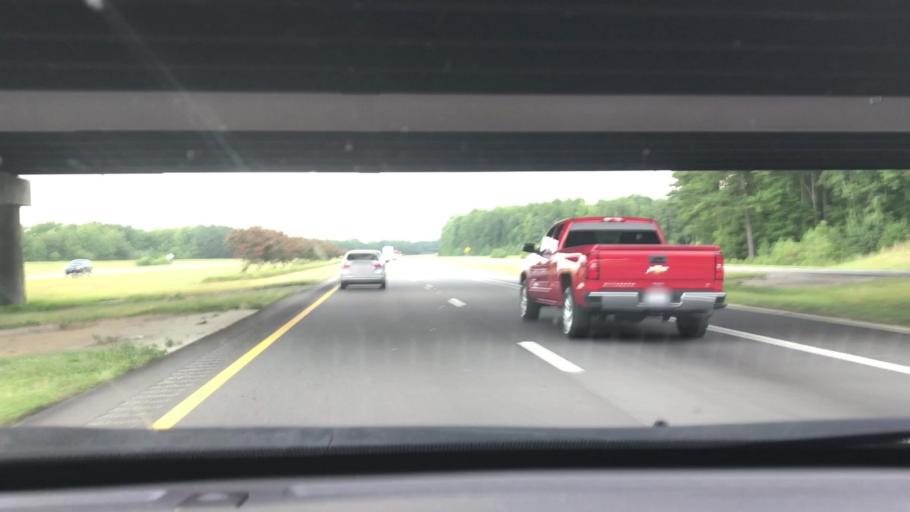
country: US
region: North Carolina
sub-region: Cumberland County
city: Vander
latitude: 35.0429
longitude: -78.8032
